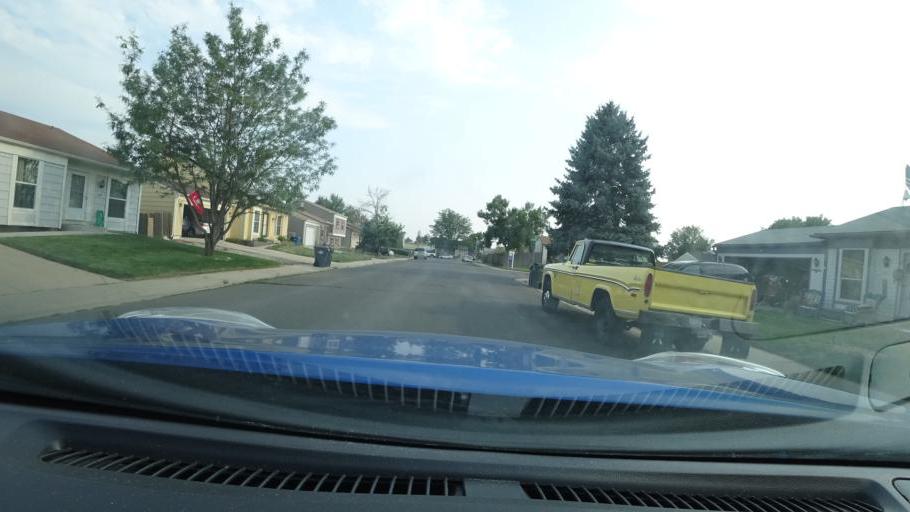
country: US
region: Colorado
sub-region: Adams County
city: Aurora
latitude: 39.7428
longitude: -104.7562
